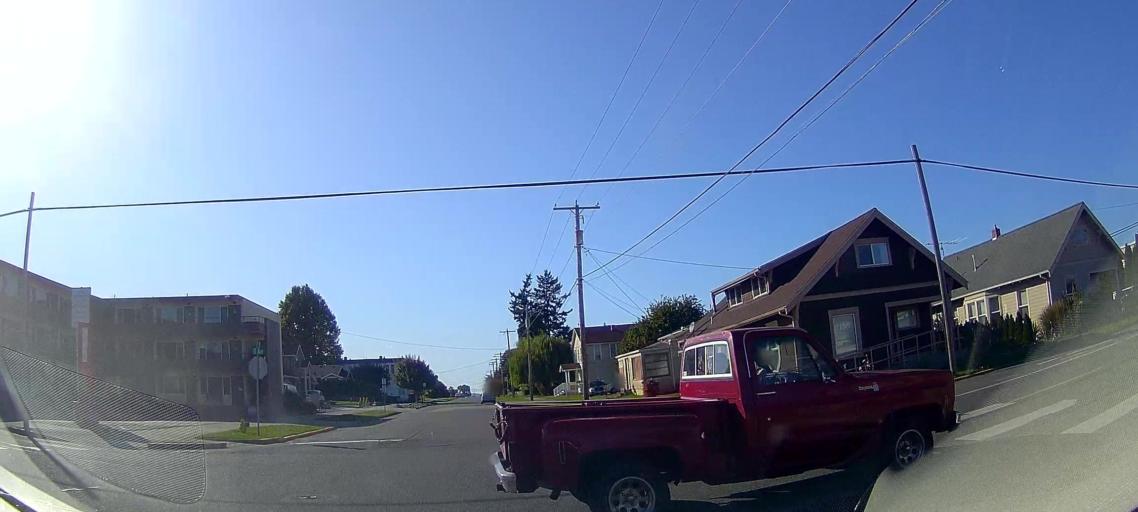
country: US
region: Washington
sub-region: Skagit County
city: Anacortes
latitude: 48.5175
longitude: -122.6140
